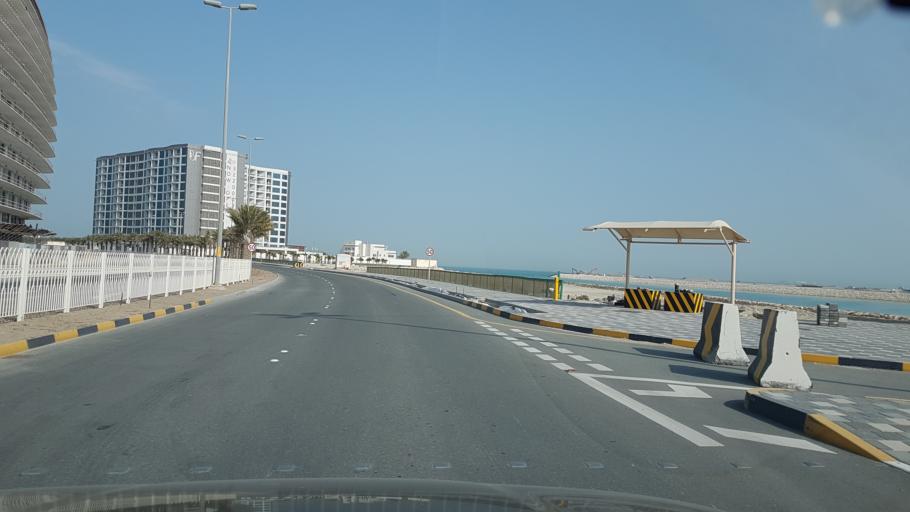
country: BH
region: Muharraq
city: Al Hadd
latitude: 26.2684
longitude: 50.6738
